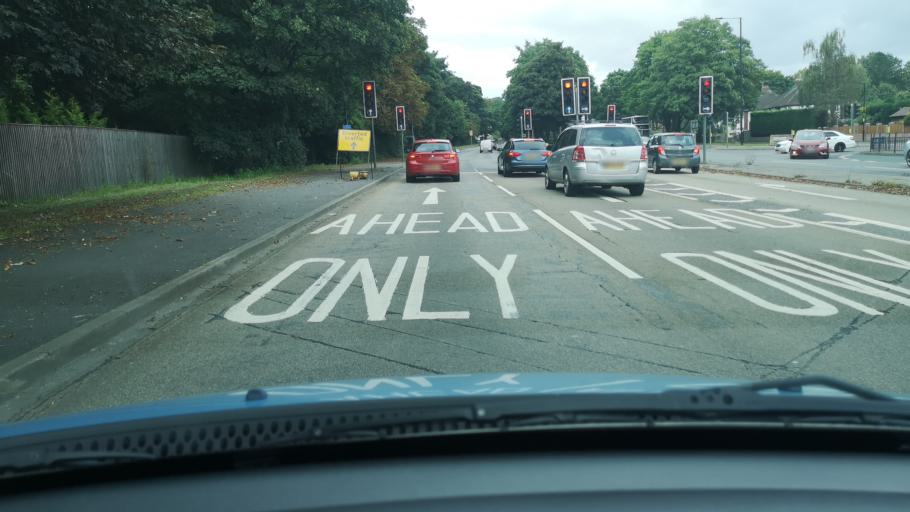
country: GB
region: England
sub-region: Doncaster
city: Bentley
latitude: 53.5463
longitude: -1.1755
